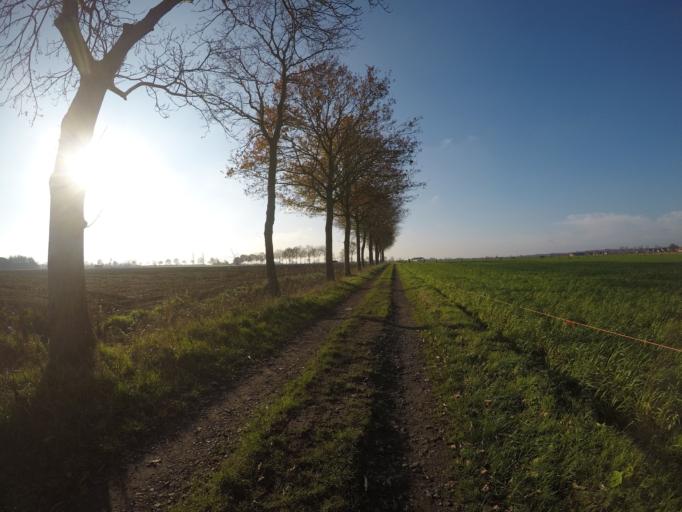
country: BE
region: Flanders
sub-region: Provincie West-Vlaanderen
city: Lichtervelde
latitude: 51.0696
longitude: 3.1783
